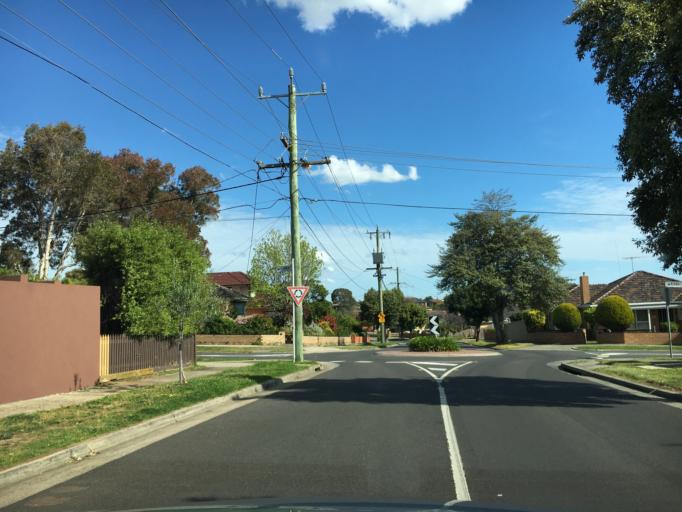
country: AU
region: Victoria
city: Clayton
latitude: -37.8995
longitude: 145.1218
